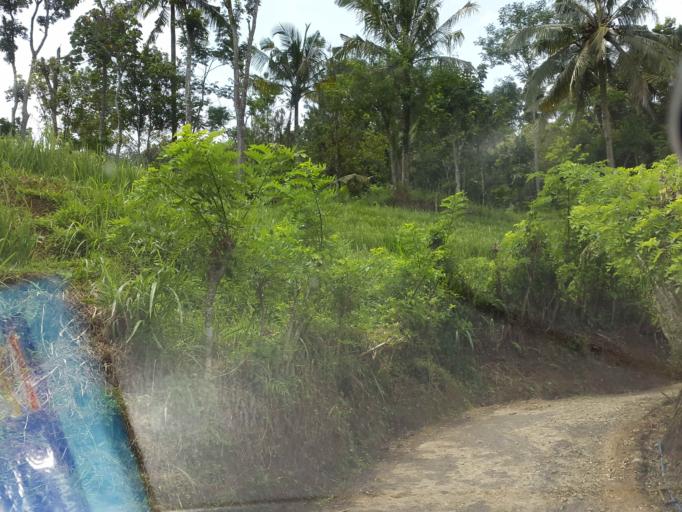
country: ID
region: Central Java
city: Muara
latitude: -7.2647
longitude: 108.8874
